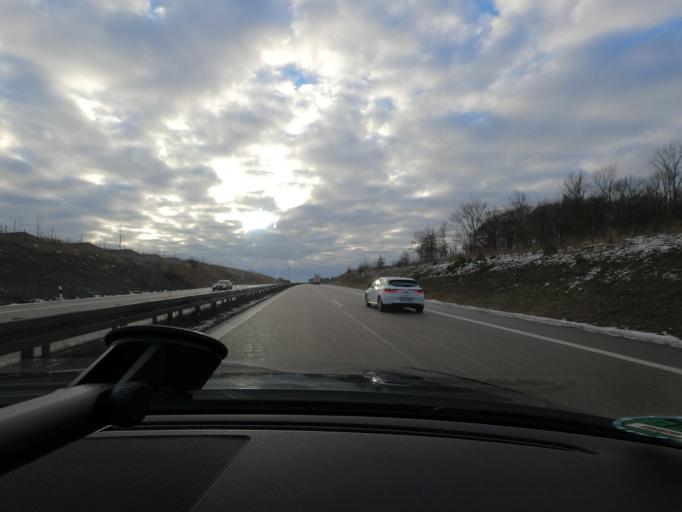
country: DE
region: Thuringia
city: Bockstadt
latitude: 50.3769
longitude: 10.9180
